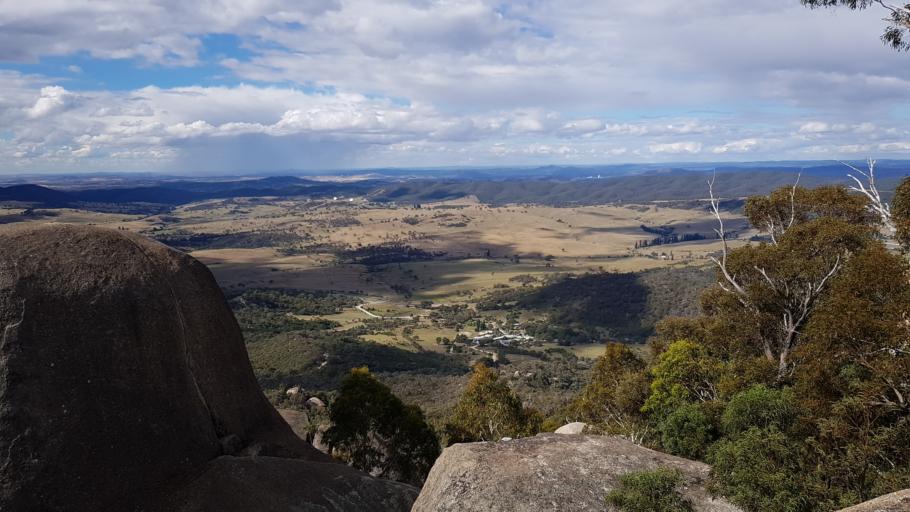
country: AU
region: Australian Capital Territory
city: Macarthur
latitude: -35.4587
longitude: 148.9478
